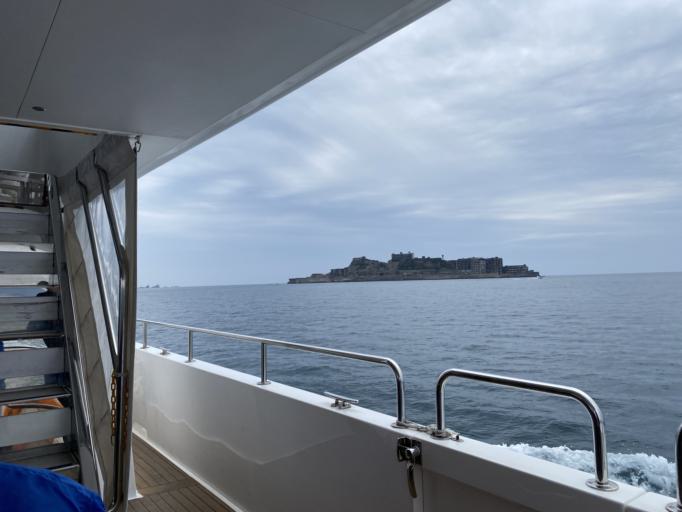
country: JP
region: Nagasaki
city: Nagasaki-shi
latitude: 32.6260
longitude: 129.7481
